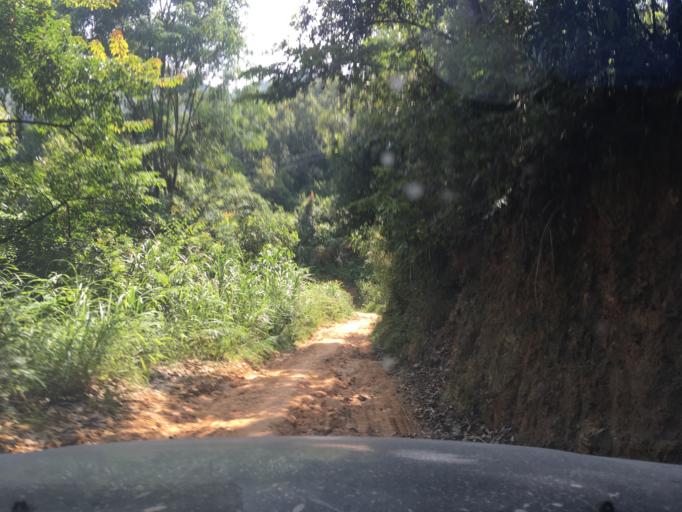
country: CN
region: Guangxi Zhuangzu Zizhiqu
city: Xinzhou
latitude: 25.0444
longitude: 105.8674
